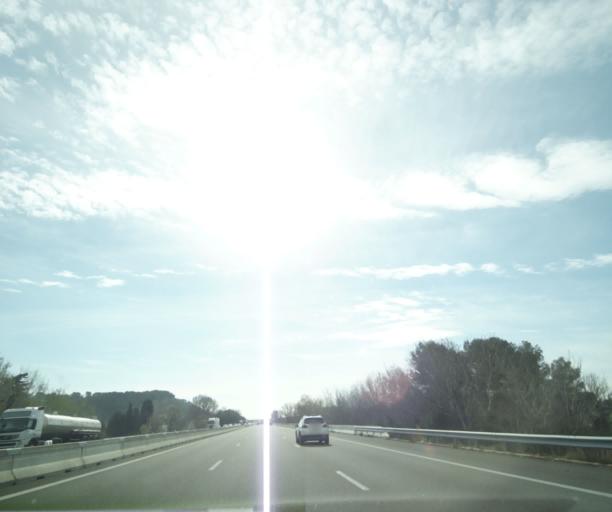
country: FR
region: Provence-Alpes-Cote d'Azur
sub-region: Departement du Vaucluse
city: Piolenc
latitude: 44.1773
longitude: 4.7550
